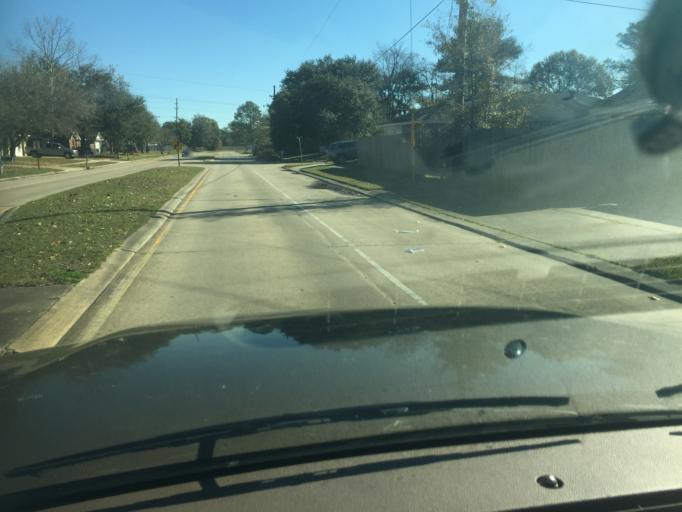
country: US
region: Louisiana
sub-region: Saint Tammany Parish
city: Slidell
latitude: 30.3017
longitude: -89.7706
